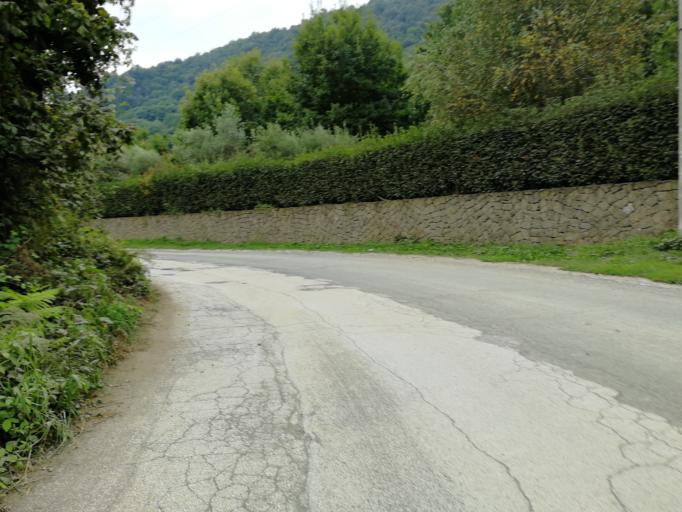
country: IT
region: Latium
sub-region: Citta metropolitana di Roma Capitale
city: Nemi
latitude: 41.7228
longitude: 12.7014
